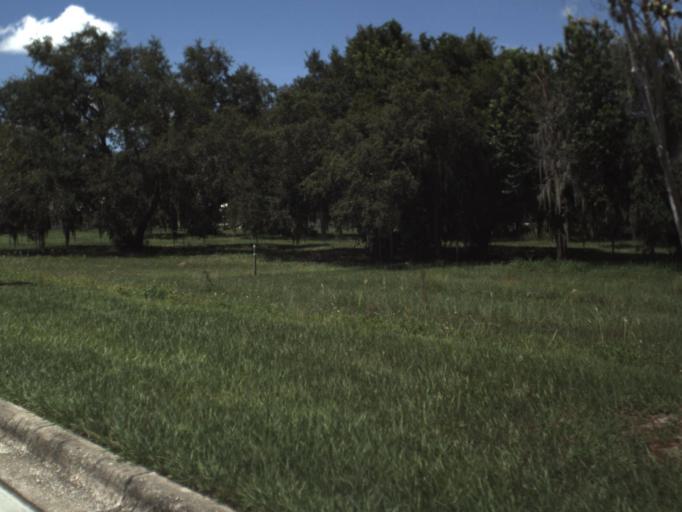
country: US
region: Florida
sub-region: Polk County
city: Inwood
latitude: 28.0463
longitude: -81.7580
